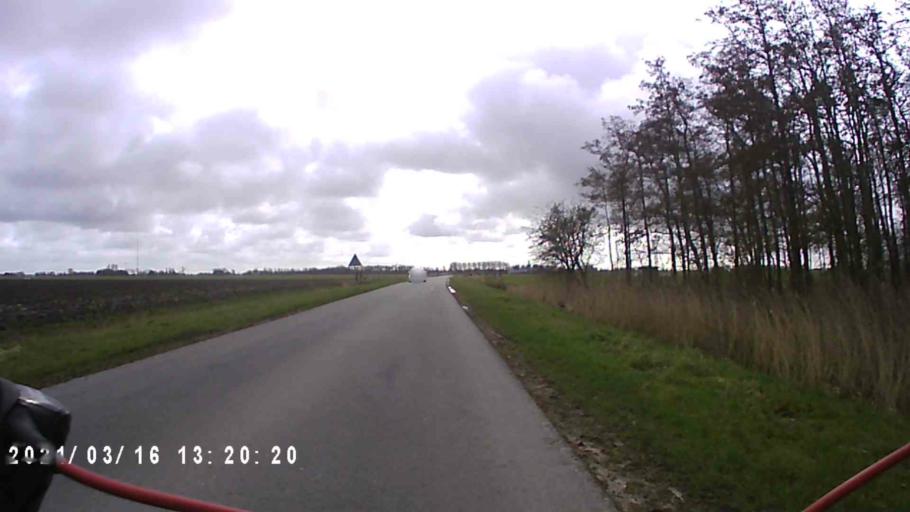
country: NL
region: Friesland
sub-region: Gemeente Het Bildt
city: Minnertsga
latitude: 53.2322
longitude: 5.5814
